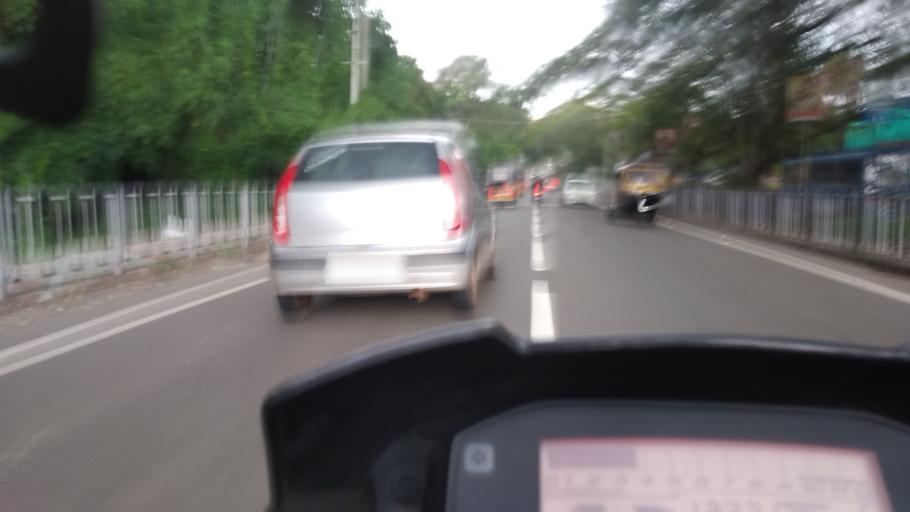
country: IN
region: Kerala
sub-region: Thiruvananthapuram
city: Attingal
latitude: 8.7080
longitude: 76.8143
